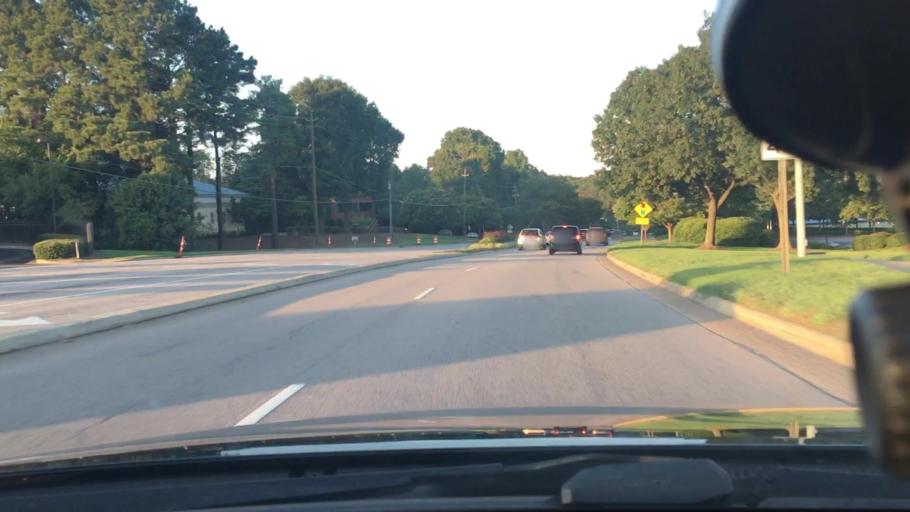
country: US
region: North Carolina
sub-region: Wake County
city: Cary
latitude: 35.7399
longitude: -78.7795
